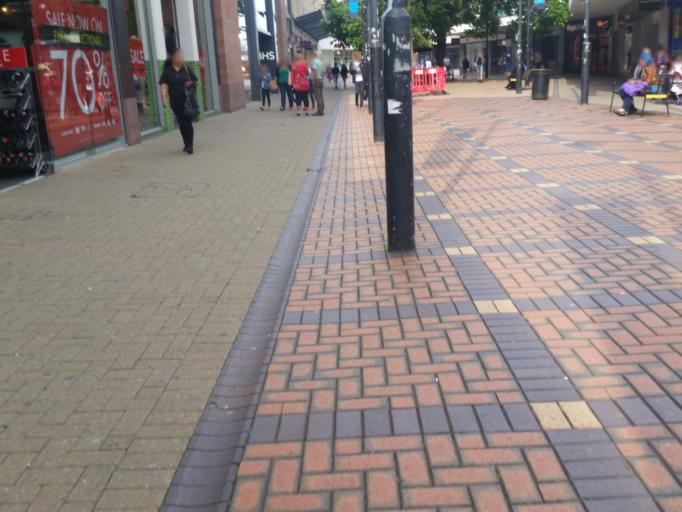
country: GB
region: England
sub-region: Borough of Swindon
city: Swindon
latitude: 51.5618
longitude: -1.7853
